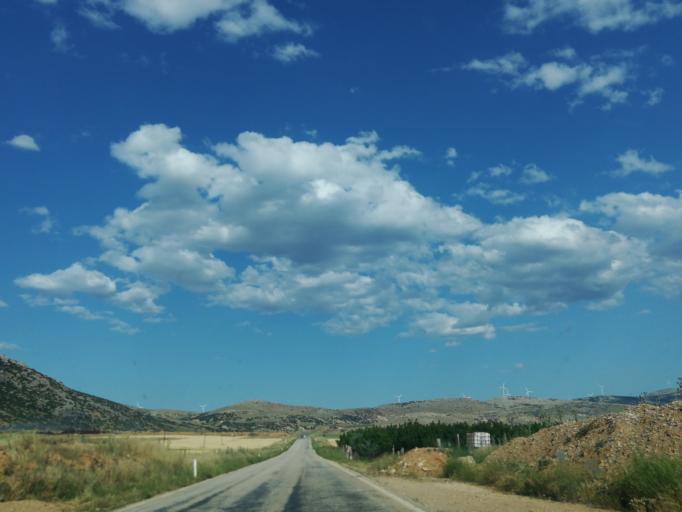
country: TR
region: Afyonkarahisar
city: Dinar
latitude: 38.1003
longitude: 30.1364
